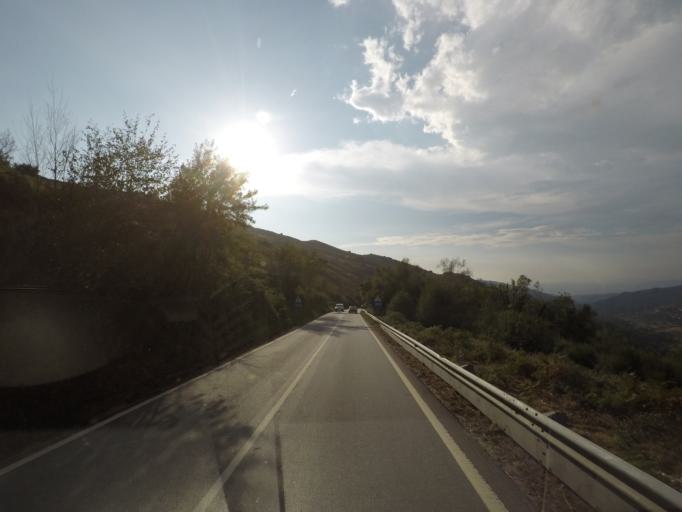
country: PT
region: Porto
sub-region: Baiao
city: Valadares
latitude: 41.1974
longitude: -7.9485
